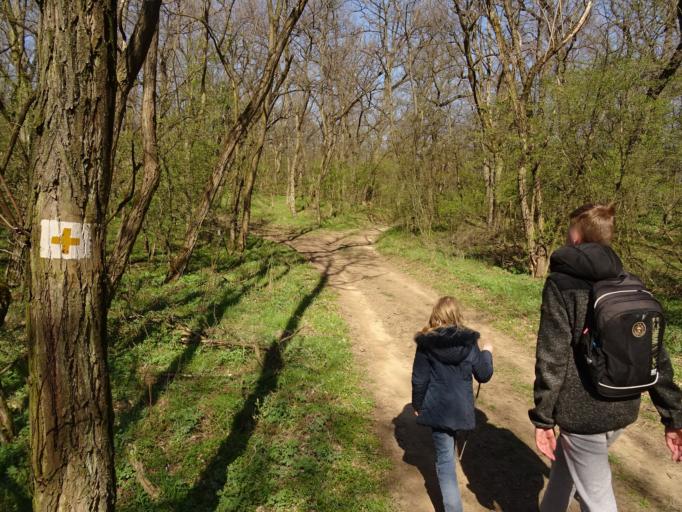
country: HU
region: Pest
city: Godollo
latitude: 47.6300
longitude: 19.3869
